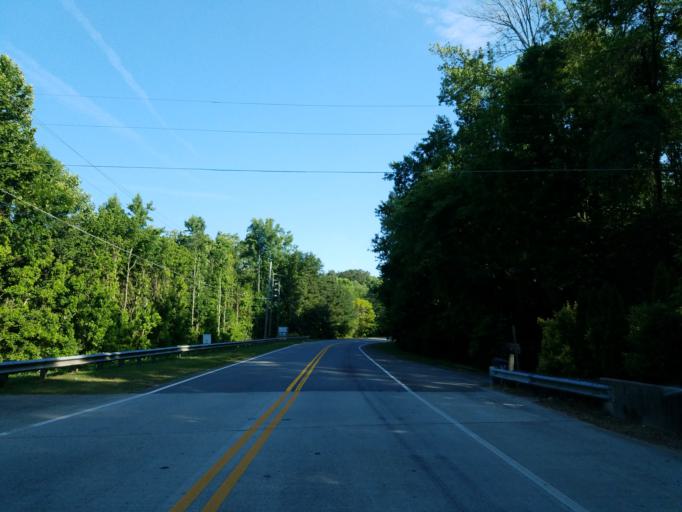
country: US
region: Georgia
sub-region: Fulton County
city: Milton
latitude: 34.1296
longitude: -84.3440
